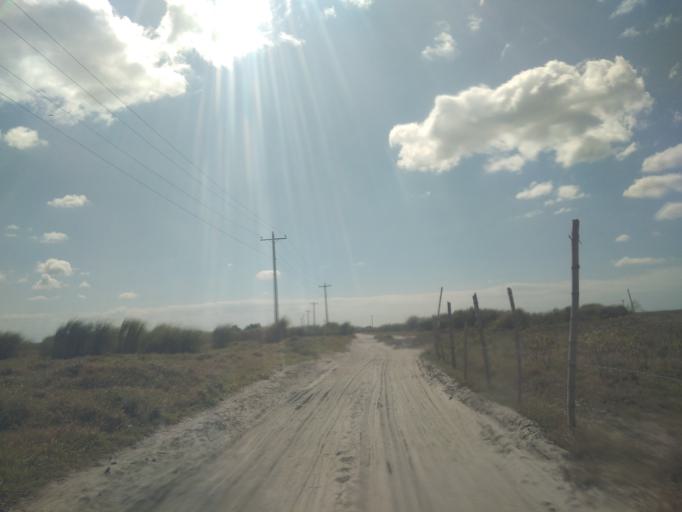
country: PH
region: Central Luzon
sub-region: Province of Pampanga
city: Balas
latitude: 15.0627
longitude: 120.5938
